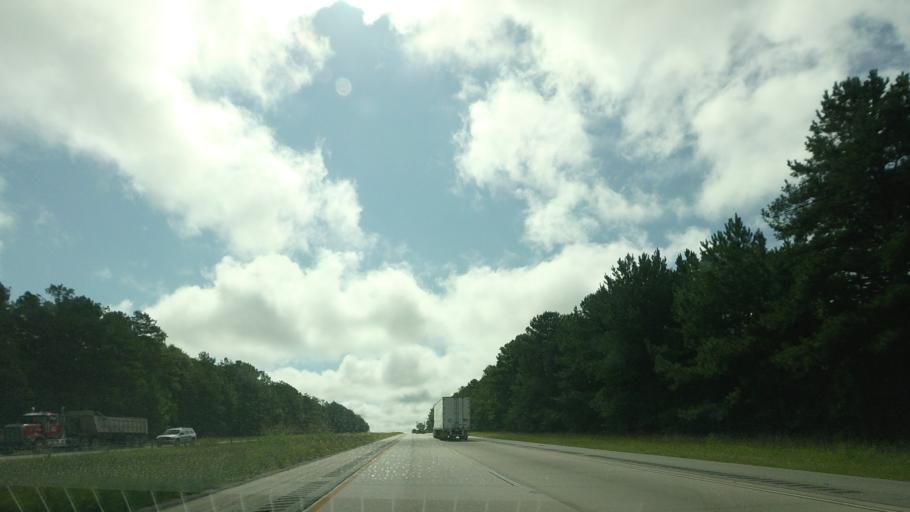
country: US
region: Georgia
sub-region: Twiggs County
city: Jeffersonville
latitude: 32.6293
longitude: -83.3807
